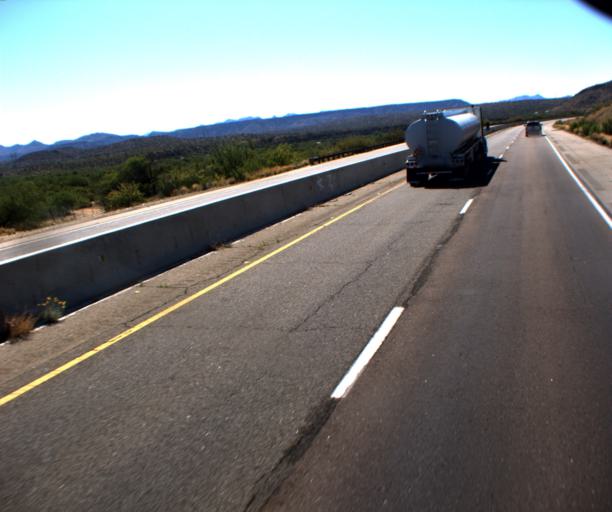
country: US
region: Arizona
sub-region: Yavapai County
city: Bagdad
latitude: 34.3814
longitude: -113.1956
